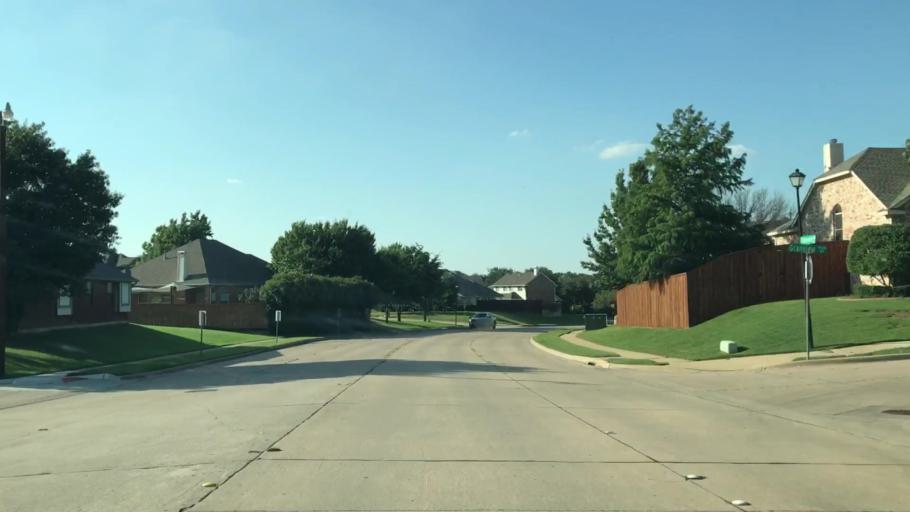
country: US
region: Texas
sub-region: Denton County
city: Lewisville
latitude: 33.0150
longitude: -97.0140
